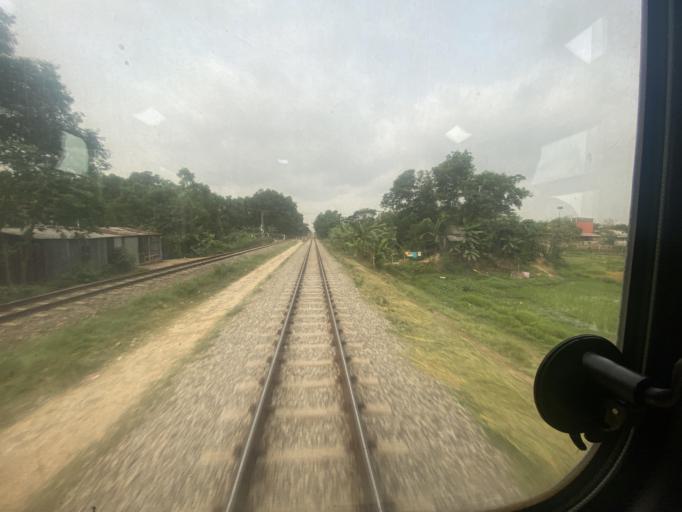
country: BD
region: Dhaka
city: Tungi
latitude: 23.9204
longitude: 90.4374
